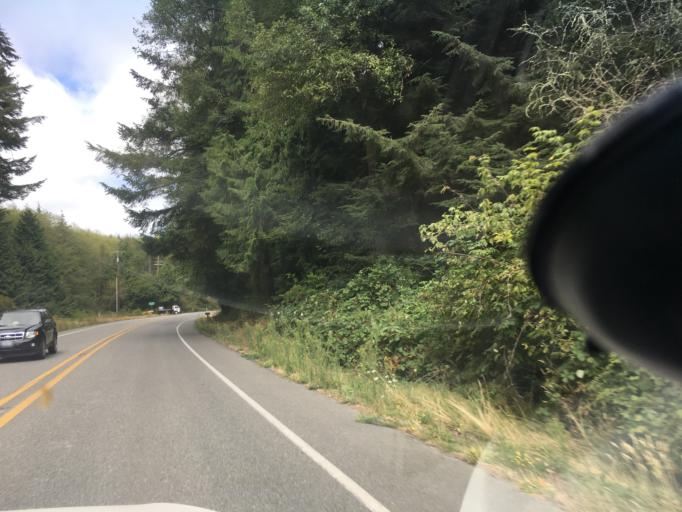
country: US
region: Washington
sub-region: Kitsap County
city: Lofall
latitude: 47.8125
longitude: -122.5822
